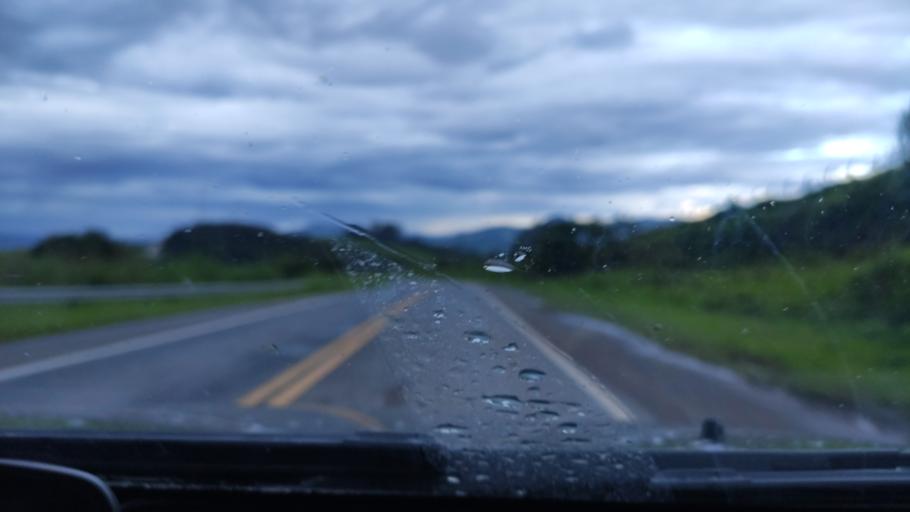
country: BR
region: Sao Paulo
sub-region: Socorro
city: Socorro
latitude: -22.6828
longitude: -46.5667
